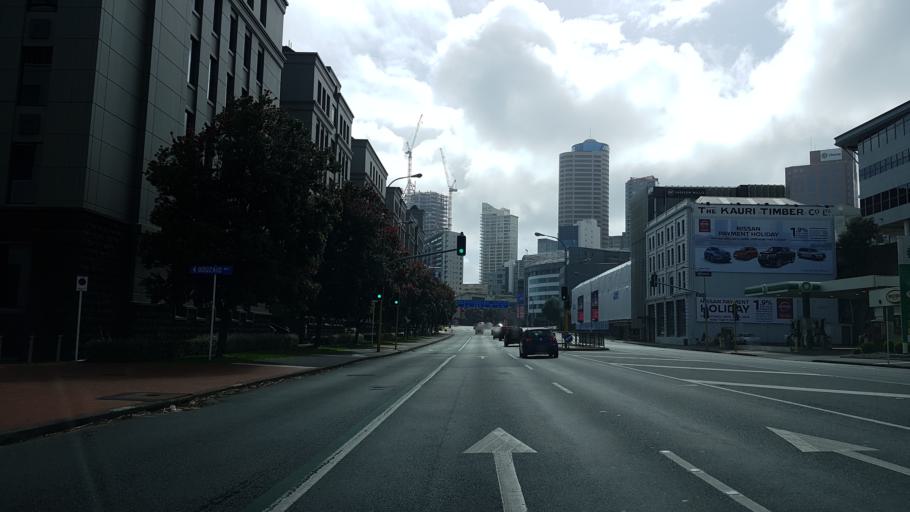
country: NZ
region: Auckland
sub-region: Auckland
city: Auckland
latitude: -36.8459
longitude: 174.7581
